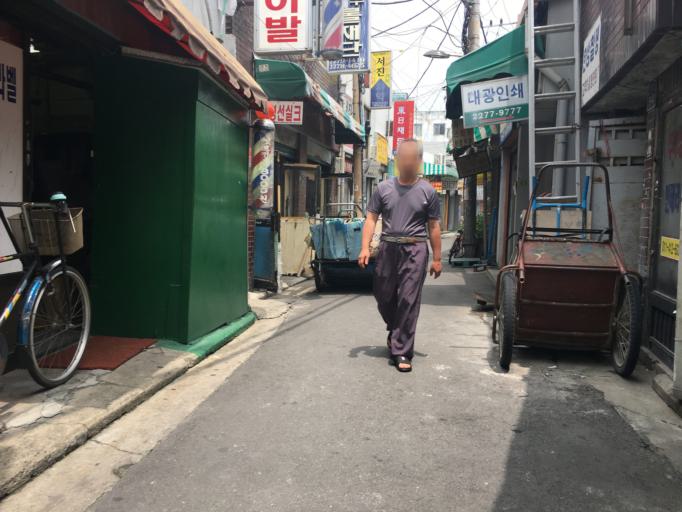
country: KR
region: Seoul
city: Seoul
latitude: 37.5679
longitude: 126.9998
